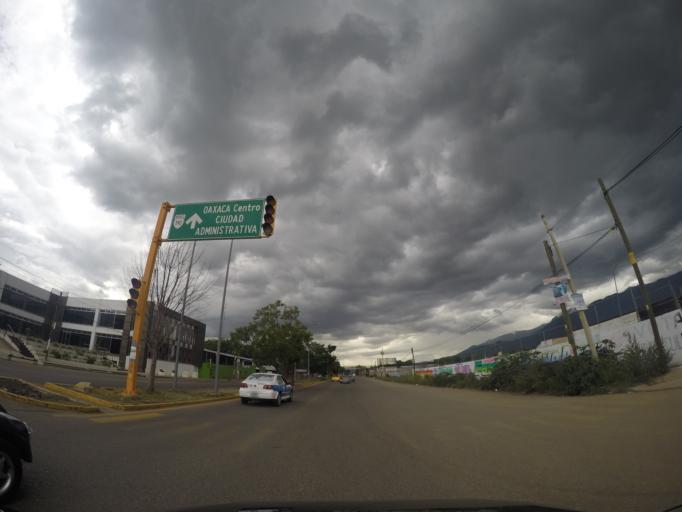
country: MX
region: Oaxaca
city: Tlalixtac de Cabrera
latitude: 17.0545
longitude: -96.6517
